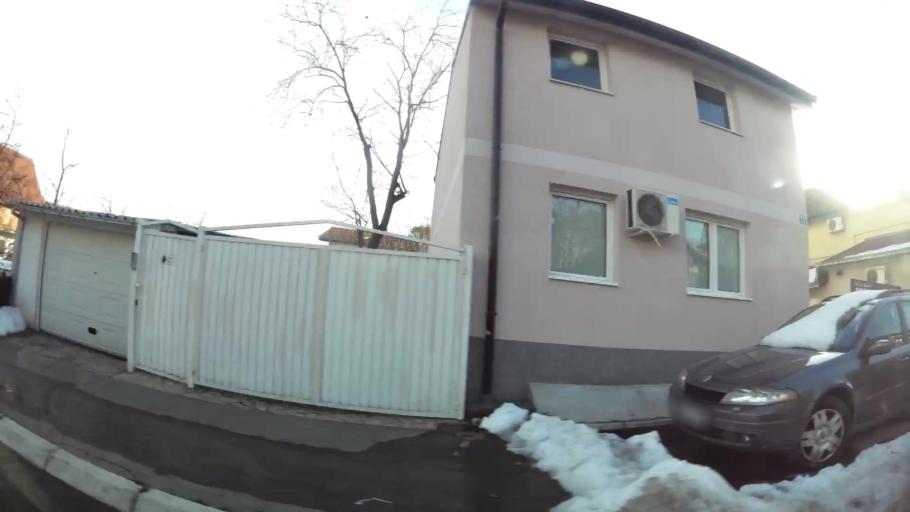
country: RS
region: Central Serbia
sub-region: Belgrade
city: Rakovica
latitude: 44.7252
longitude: 20.4308
